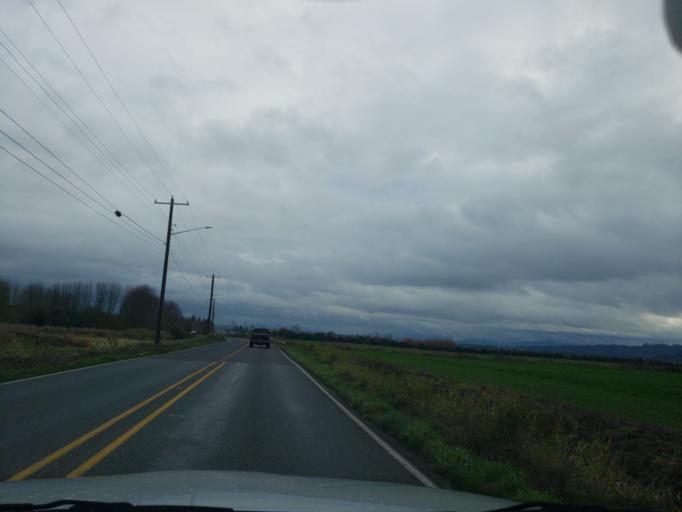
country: US
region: Washington
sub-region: Snohomish County
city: Snohomish
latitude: 47.8992
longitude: -122.1327
